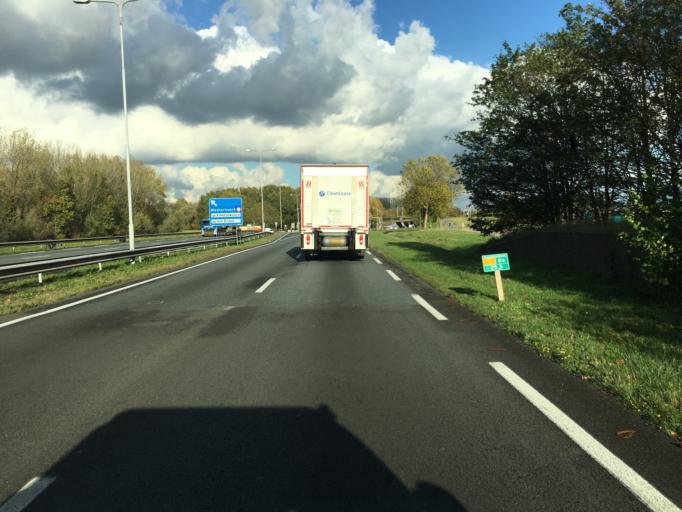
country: NL
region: Gelderland
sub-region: Gemeente Westervoort
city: Westervoort
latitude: 51.9677
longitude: 5.9526
